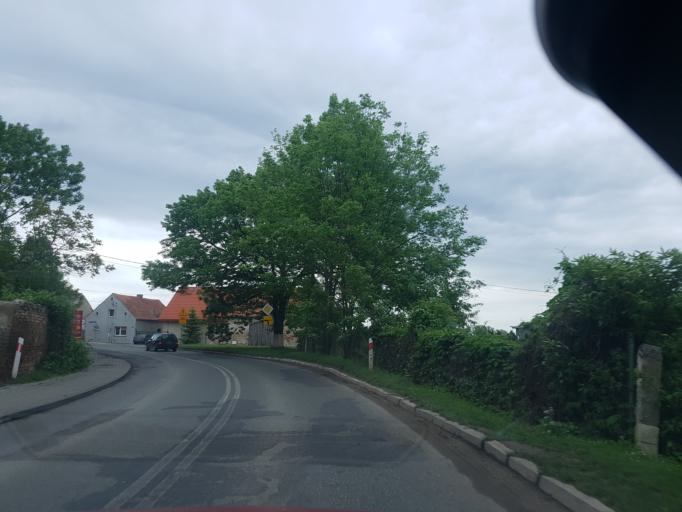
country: PL
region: Lower Silesian Voivodeship
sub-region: Powiat wroclawski
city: Zorawina
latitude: 50.9263
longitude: 17.0374
